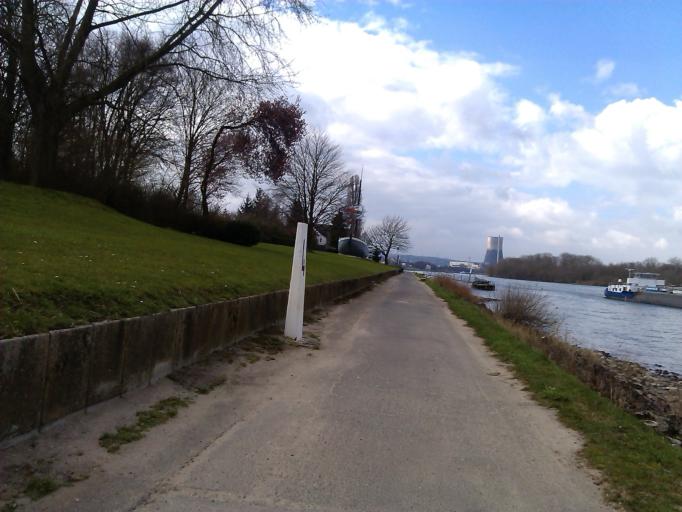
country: DE
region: Rheinland-Pfalz
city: Urmitz
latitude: 50.4188
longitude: 7.5238
